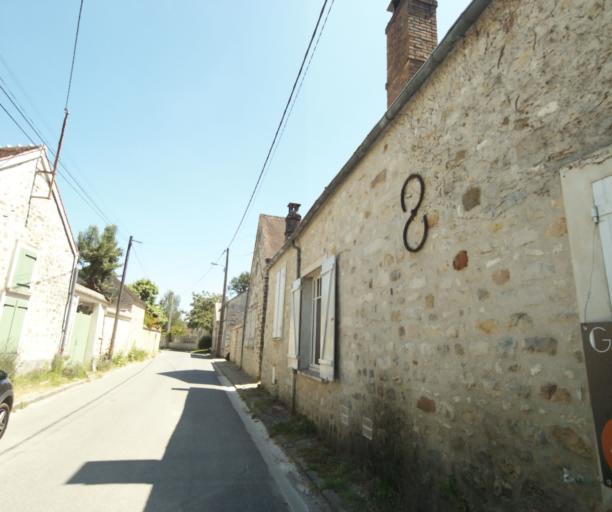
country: FR
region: Ile-de-France
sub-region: Departement de Seine-et-Marne
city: Noisy-sur-Ecole
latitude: 48.3679
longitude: 2.5057
